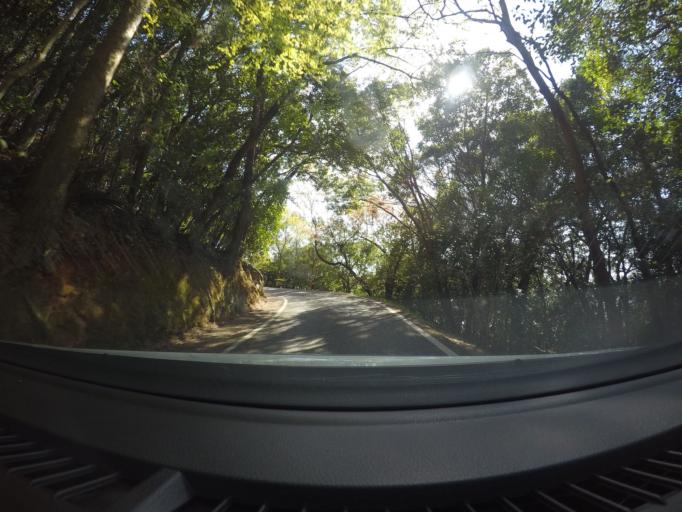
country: JP
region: Kochi
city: Kochi-shi
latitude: 33.5474
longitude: 133.5728
